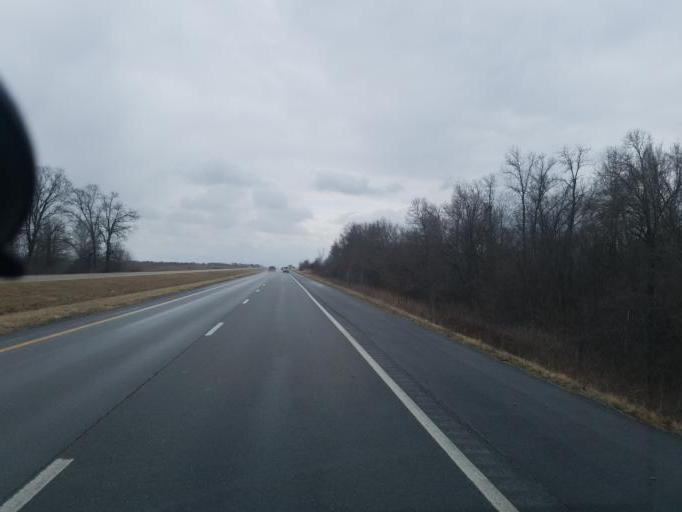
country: US
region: Missouri
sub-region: Randolph County
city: Moberly
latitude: 39.3502
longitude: -92.3961
